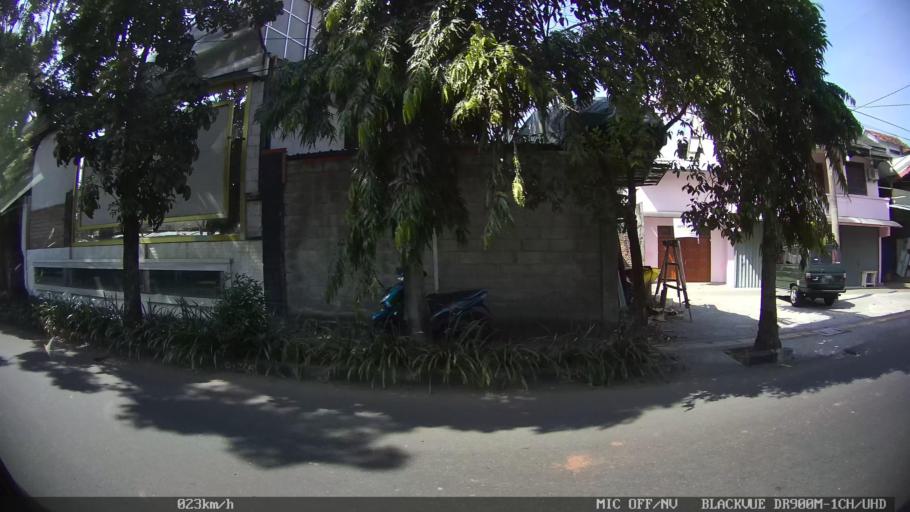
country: ID
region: Daerah Istimewa Yogyakarta
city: Yogyakarta
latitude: -7.8254
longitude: 110.3762
